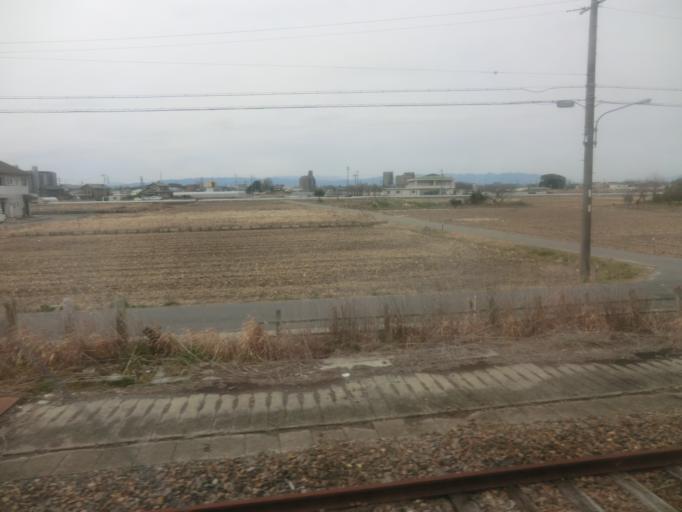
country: JP
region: Aichi
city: Inazawa
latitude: 35.2621
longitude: 136.8162
